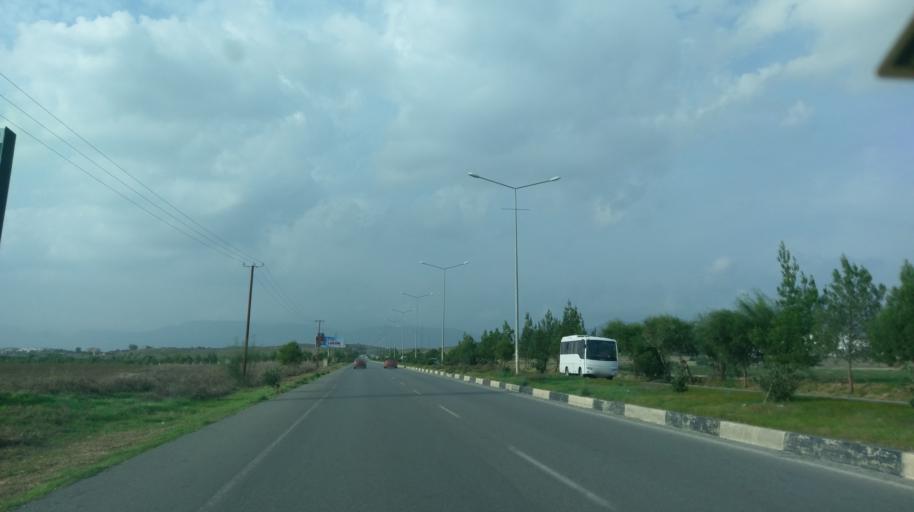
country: CY
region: Lefkosia
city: Nicosia
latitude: 35.2187
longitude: 33.3174
